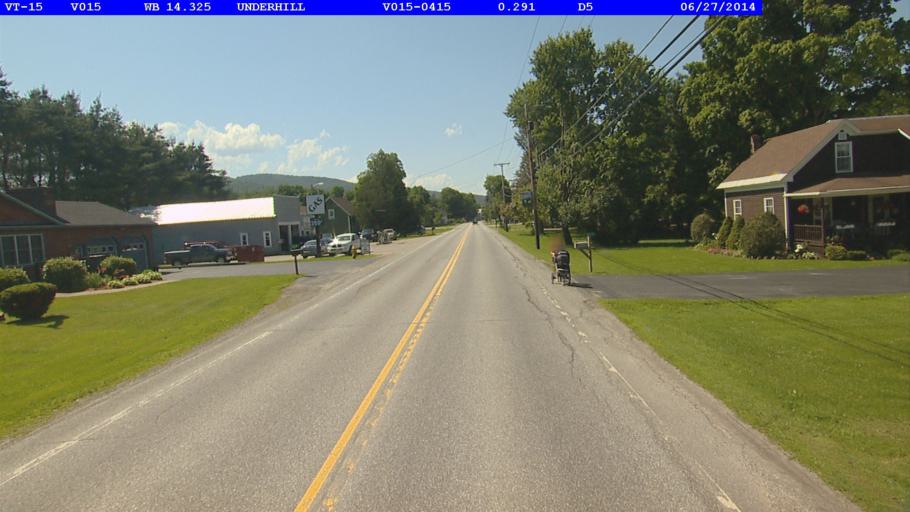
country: US
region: Vermont
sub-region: Chittenden County
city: Jericho
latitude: 44.5294
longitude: -72.9449
